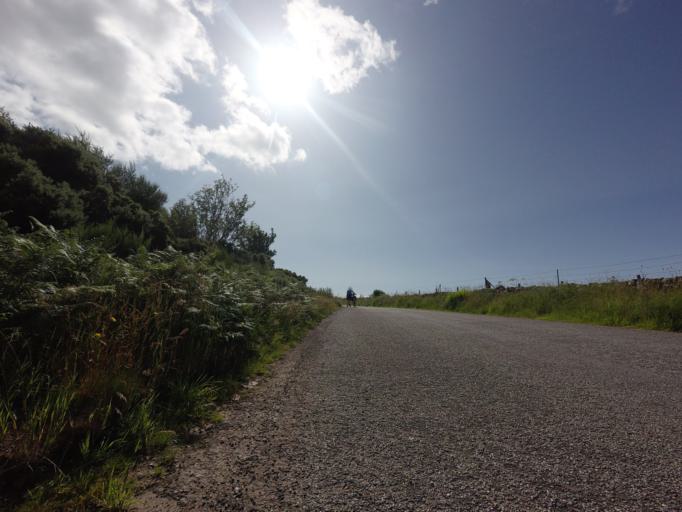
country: GB
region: Scotland
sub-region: Highland
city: Nairn
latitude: 57.5318
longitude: -3.8640
